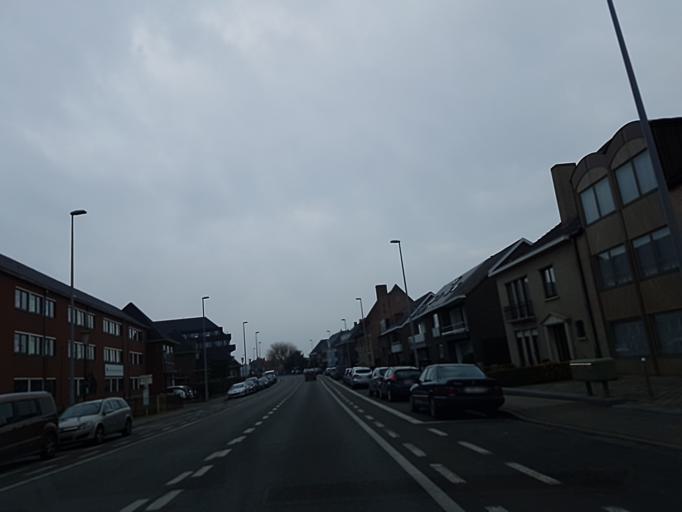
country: BE
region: Flanders
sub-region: Provincie Oost-Vlaanderen
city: Deinze
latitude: 50.9860
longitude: 3.5306
